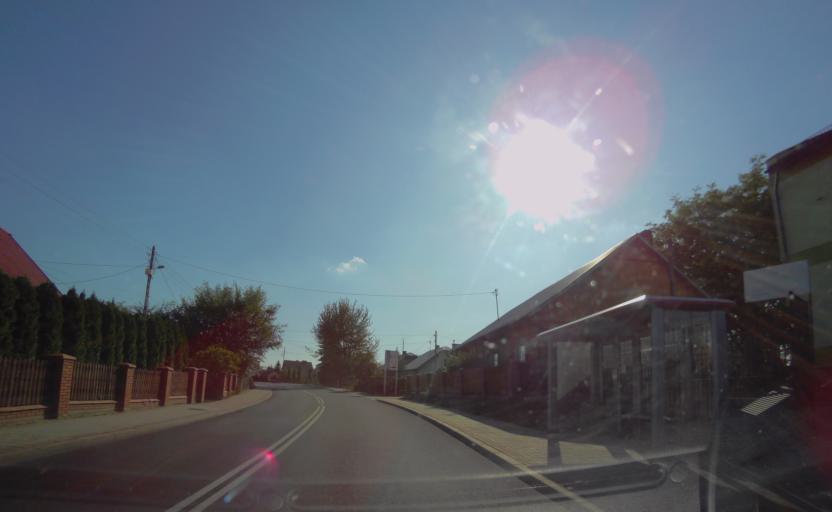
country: PL
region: Subcarpathian Voivodeship
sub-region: Powiat lezajski
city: Stare Miasto
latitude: 50.2884
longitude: 22.4290
